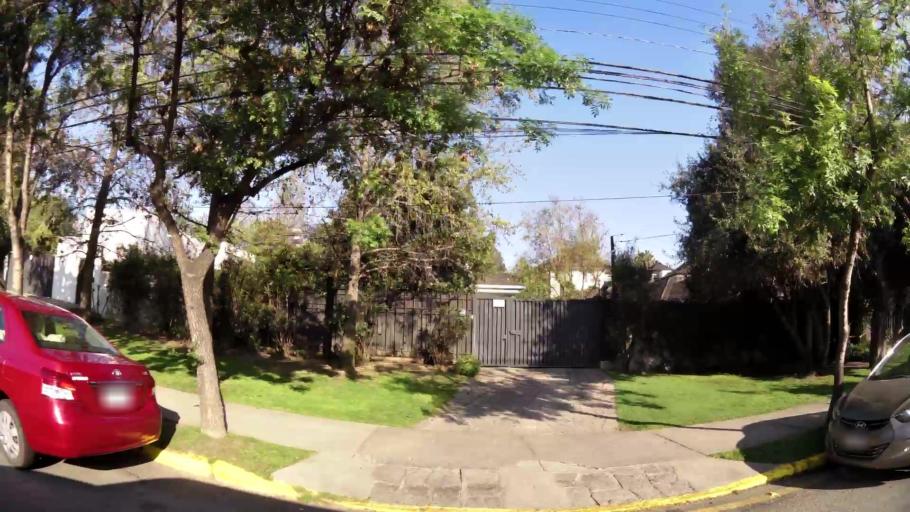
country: CL
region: Santiago Metropolitan
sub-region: Provincia de Santiago
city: Villa Presidente Frei, Nunoa, Santiago, Chile
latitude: -33.3755
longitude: -70.5290
